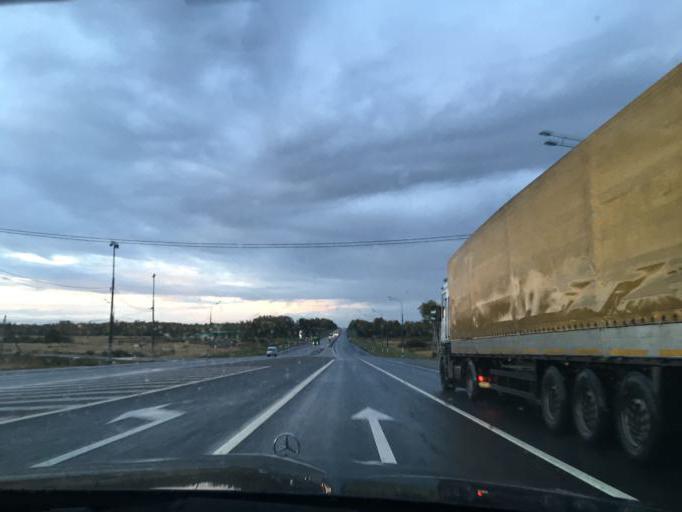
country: RU
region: Smolensk
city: Safonovo
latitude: 55.1573
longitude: 33.3656
